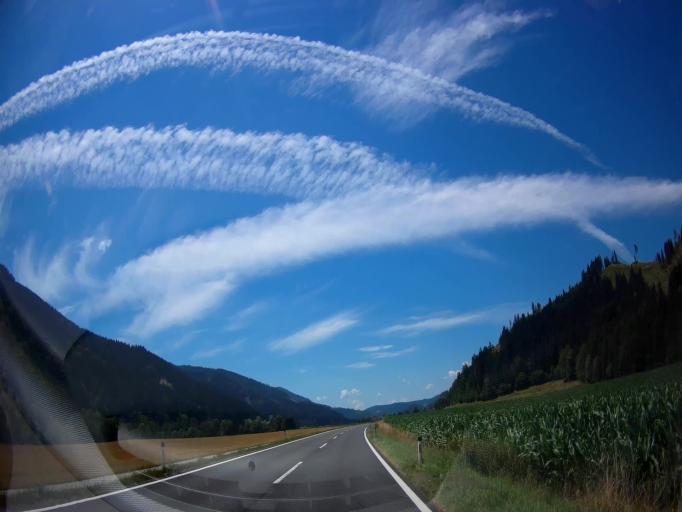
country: AT
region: Carinthia
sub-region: Politischer Bezirk Sankt Veit an der Glan
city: Micheldorf
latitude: 46.9036
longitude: 14.3977
